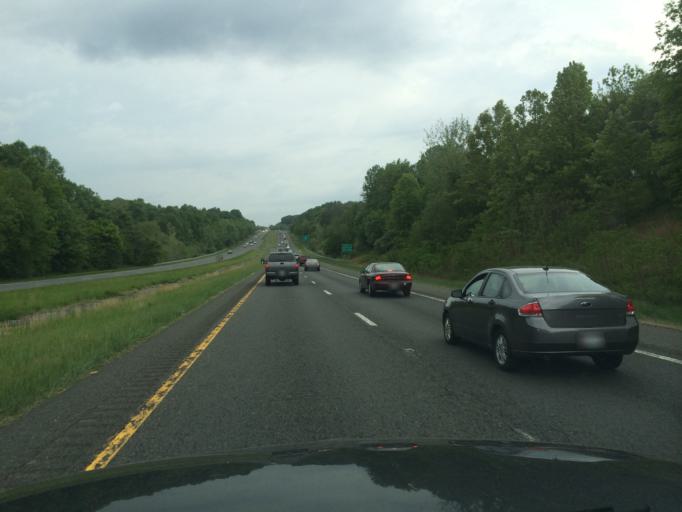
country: US
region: Maryland
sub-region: Howard County
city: Highland
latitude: 39.1981
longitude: -76.9266
